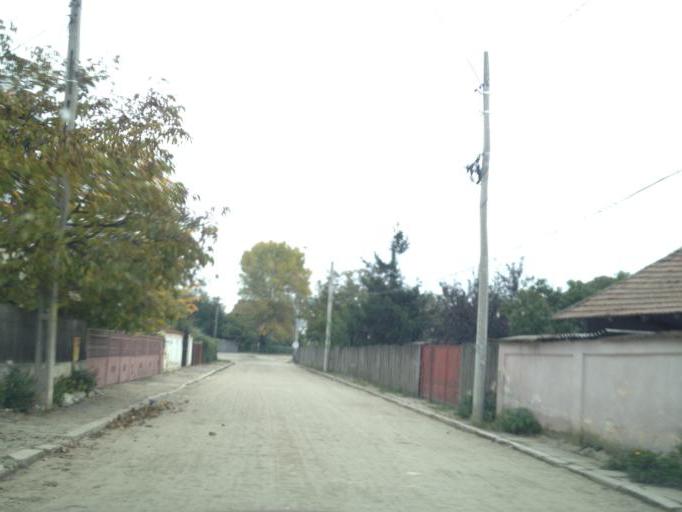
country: RO
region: Dolj
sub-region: Municipiul Craiova
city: Popoveni
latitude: 44.2920
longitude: 23.8047
